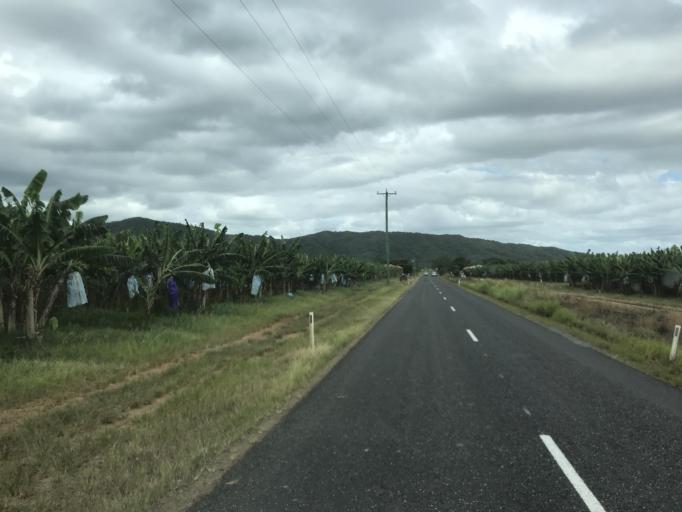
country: AU
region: Queensland
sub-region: Cassowary Coast
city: Innisfail
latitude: -17.6210
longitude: 146.0242
